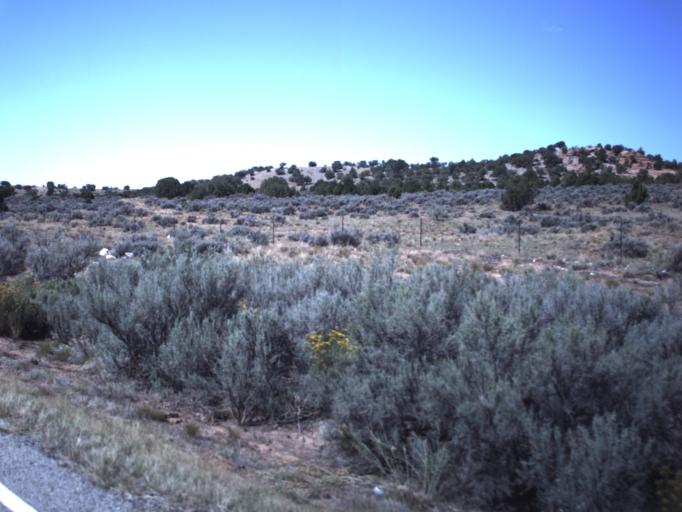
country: US
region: Utah
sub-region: Grand County
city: Moab
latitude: 38.3046
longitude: -109.3869
